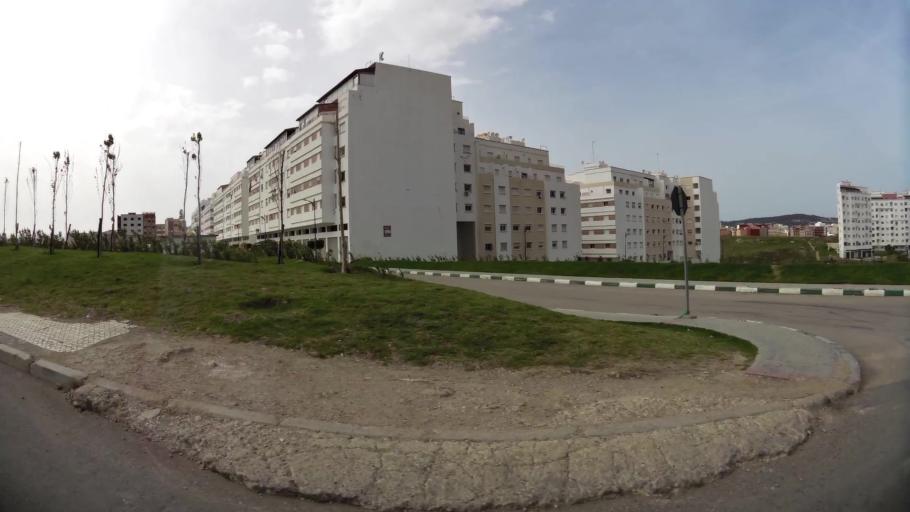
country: MA
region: Tanger-Tetouan
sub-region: Tanger-Assilah
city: Boukhalef
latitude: 35.7441
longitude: -5.8537
